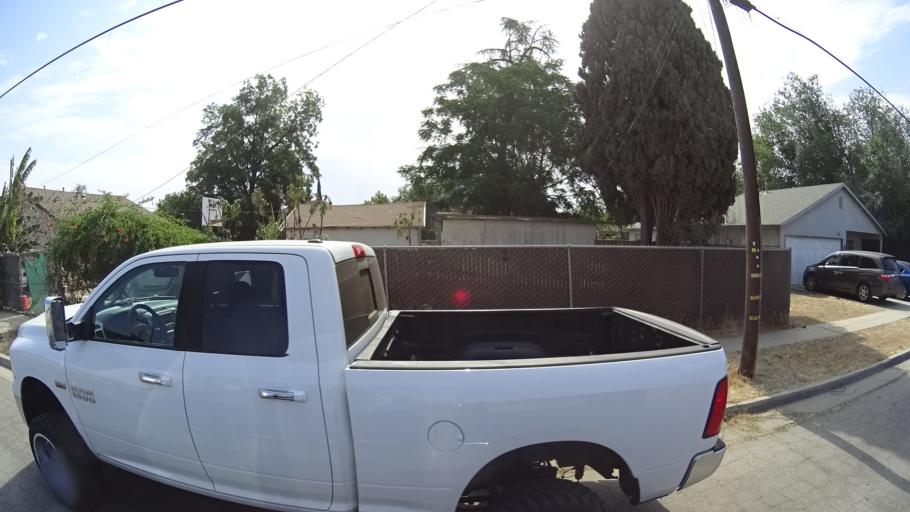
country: US
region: California
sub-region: Fresno County
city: West Park
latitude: 36.7336
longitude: -119.8153
